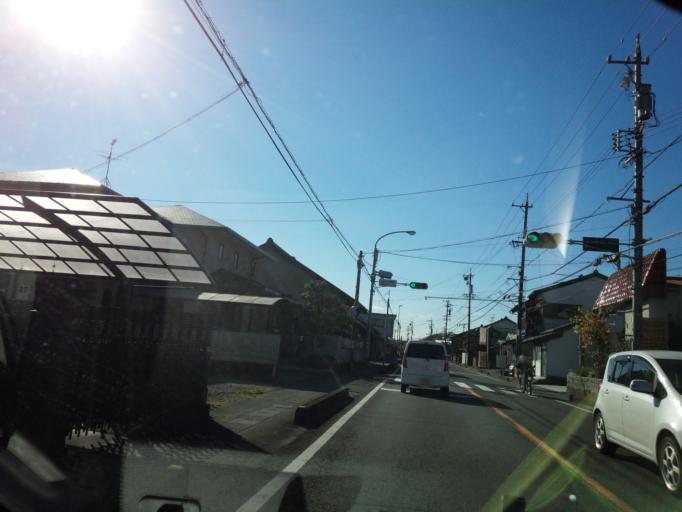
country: JP
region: Shizuoka
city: Shizuoka-shi
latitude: 35.0443
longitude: 138.5013
